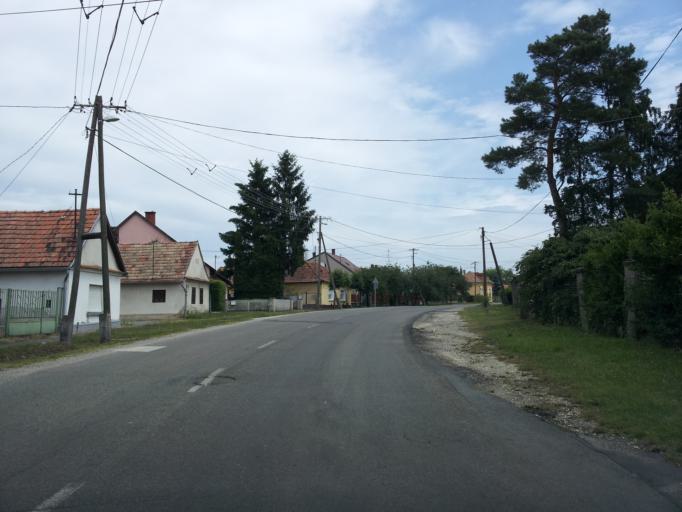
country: HU
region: Vas
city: Vasvar
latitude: 47.0511
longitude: 16.8043
